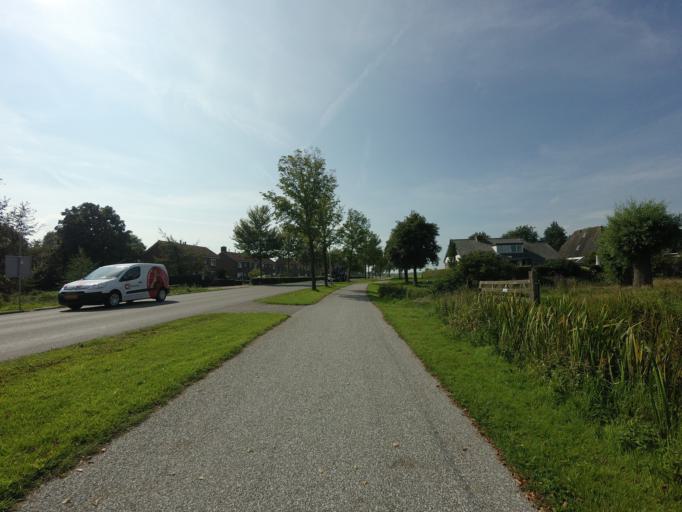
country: NL
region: Friesland
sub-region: Sudwest Fryslan
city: Heeg
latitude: 52.9786
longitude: 5.6483
